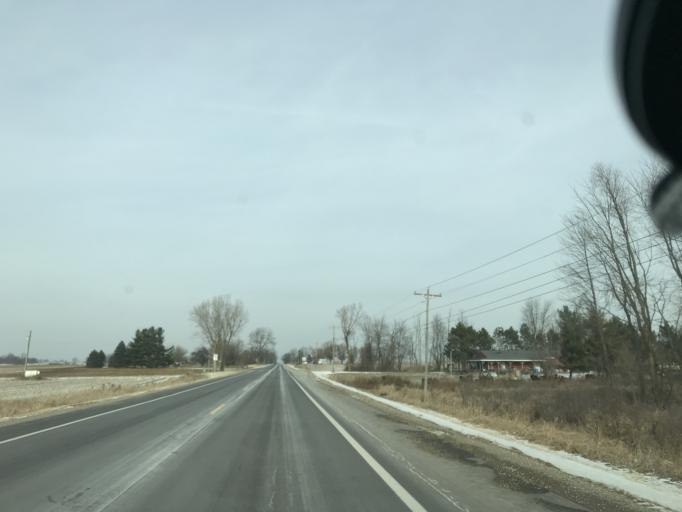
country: US
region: Michigan
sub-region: Ionia County
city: Lake Odessa
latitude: 42.8557
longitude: -85.0749
